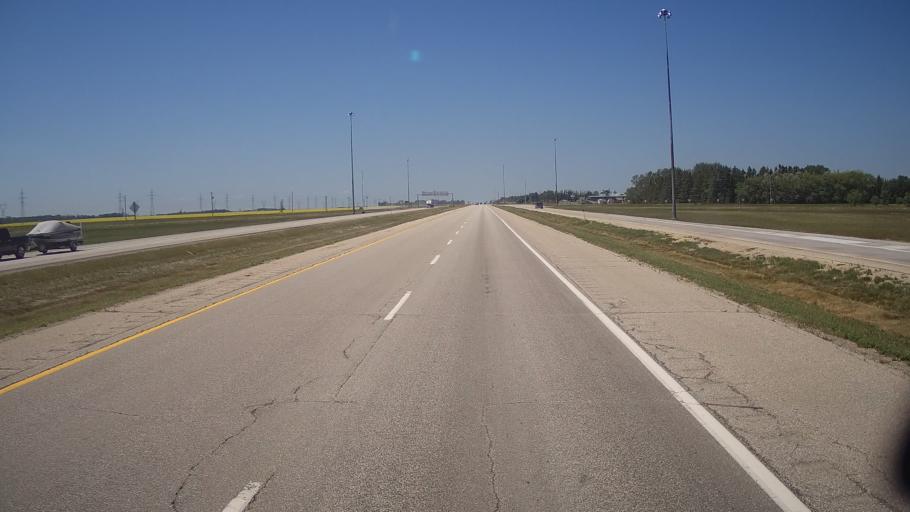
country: CA
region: Manitoba
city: Winnipeg
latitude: 49.9900
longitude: -97.2308
